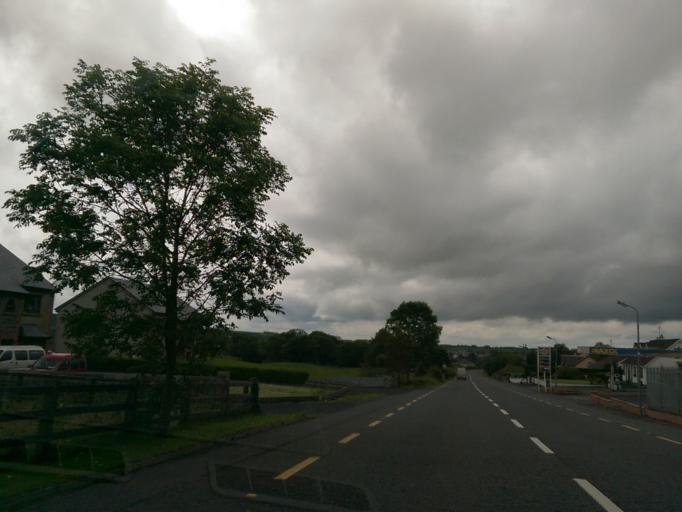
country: IE
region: Munster
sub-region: An Clar
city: Ennis
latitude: 52.7546
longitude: -9.1342
